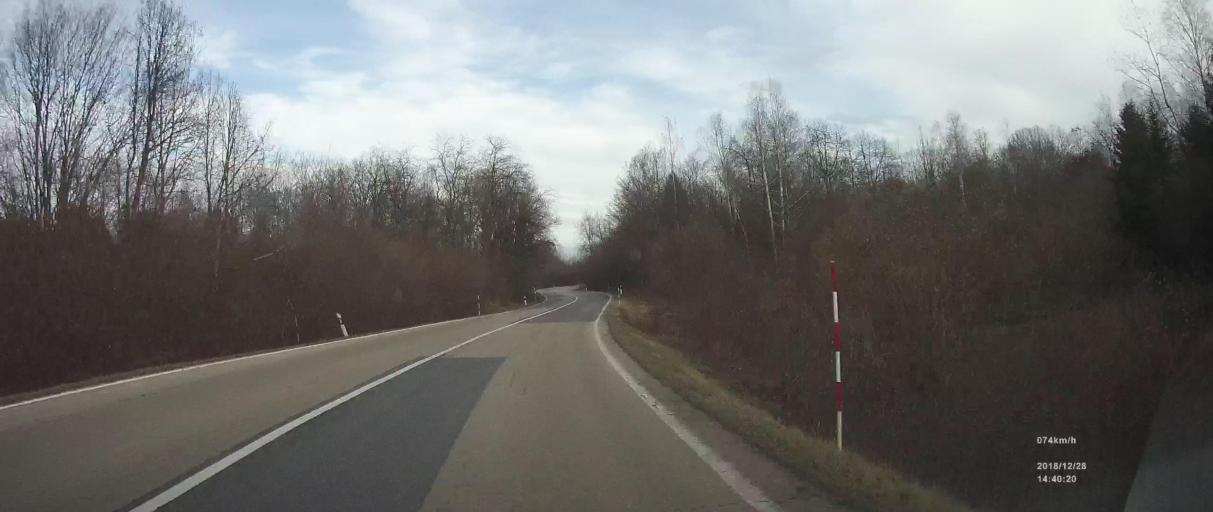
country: SI
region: Crnomelj
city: Crnomelj
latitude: 45.4326
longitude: 15.2428
